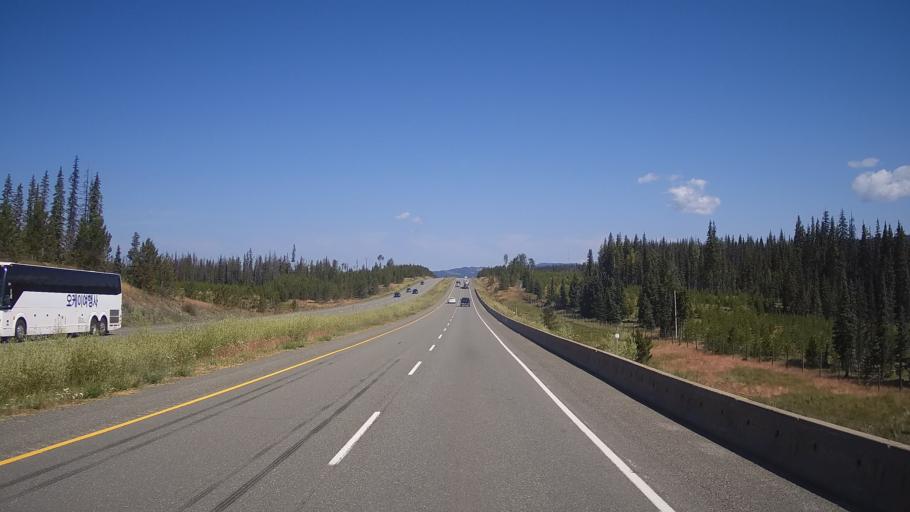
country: CA
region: British Columbia
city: Logan Lake
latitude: 50.3921
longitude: -120.6239
